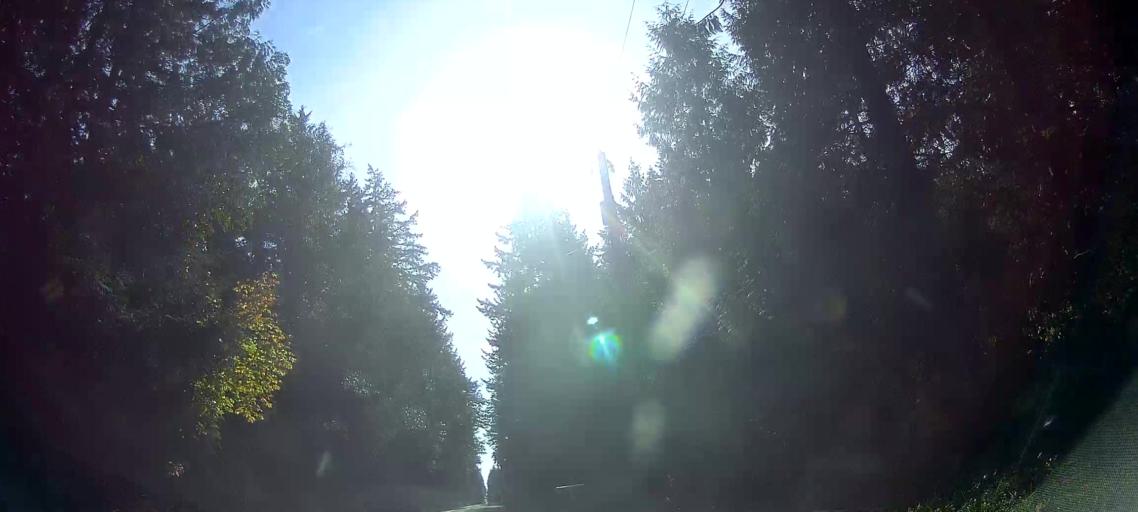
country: US
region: Washington
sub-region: Island County
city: Camano
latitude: 48.2218
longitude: -122.4558
